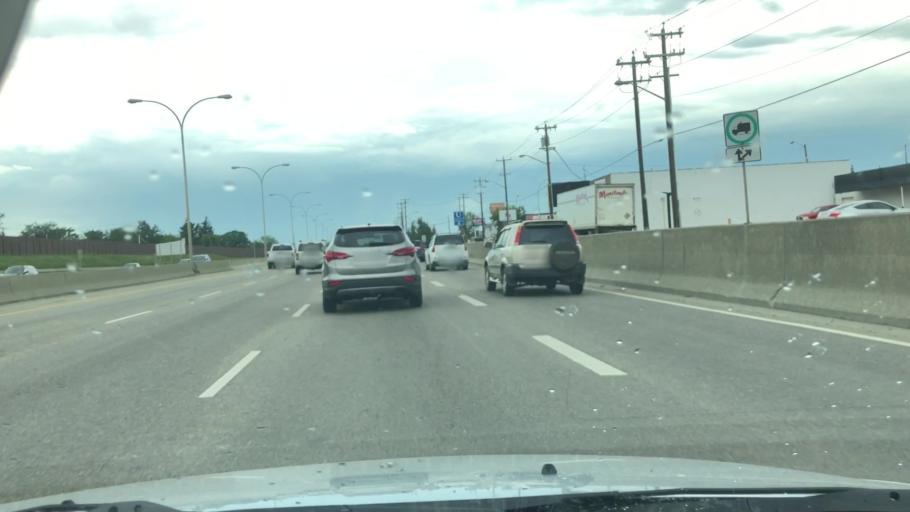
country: CA
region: Alberta
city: Edmonton
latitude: 53.5805
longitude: -113.4592
